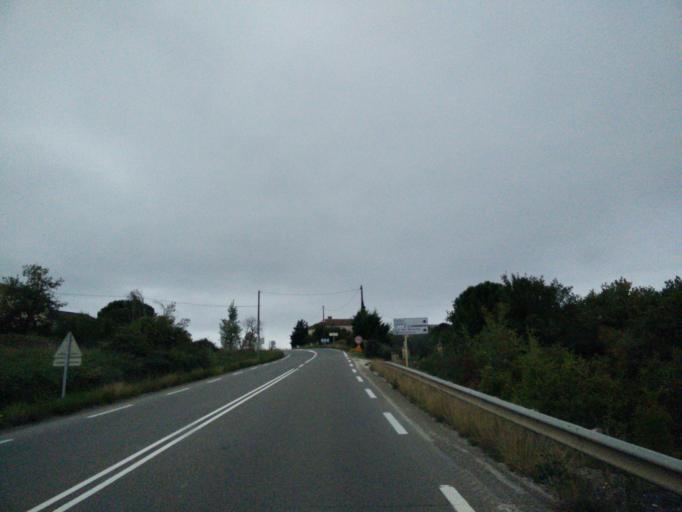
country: FR
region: Midi-Pyrenees
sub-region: Departement du Lot
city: Pradines
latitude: 44.5205
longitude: 1.3512
